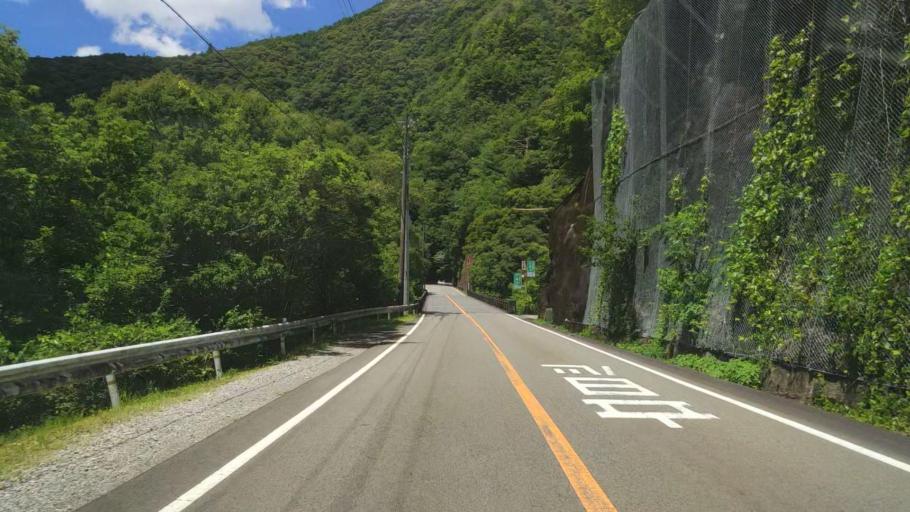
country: JP
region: Mie
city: Owase
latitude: 33.9982
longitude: 136.0177
